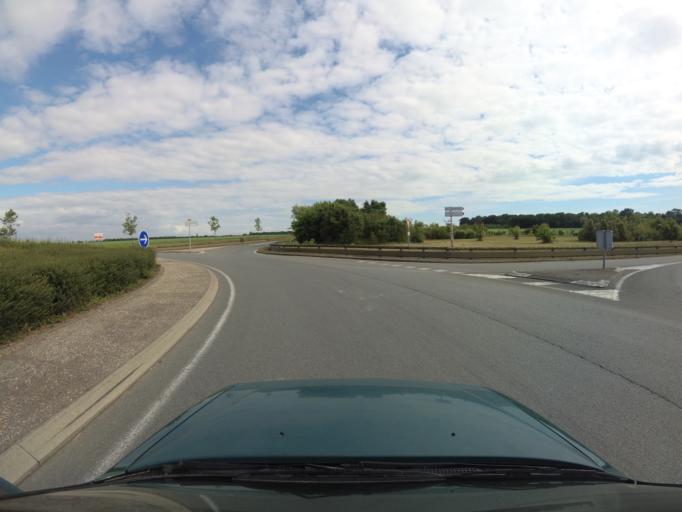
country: FR
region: Poitou-Charentes
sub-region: Departement de la Charente-Maritime
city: Saint-Xandre
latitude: 46.1952
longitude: -1.0955
